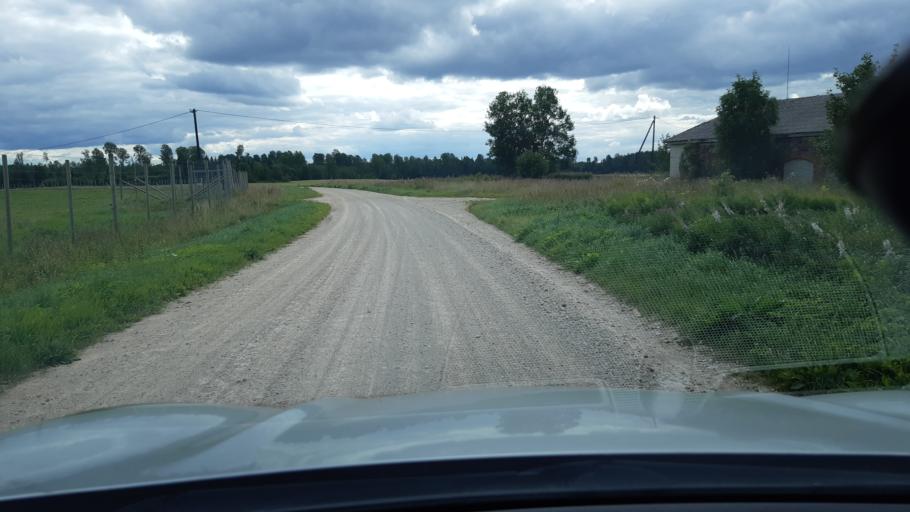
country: EE
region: Paernumaa
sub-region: Vaendra vald (alev)
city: Vandra
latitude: 58.7789
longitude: 25.0520
